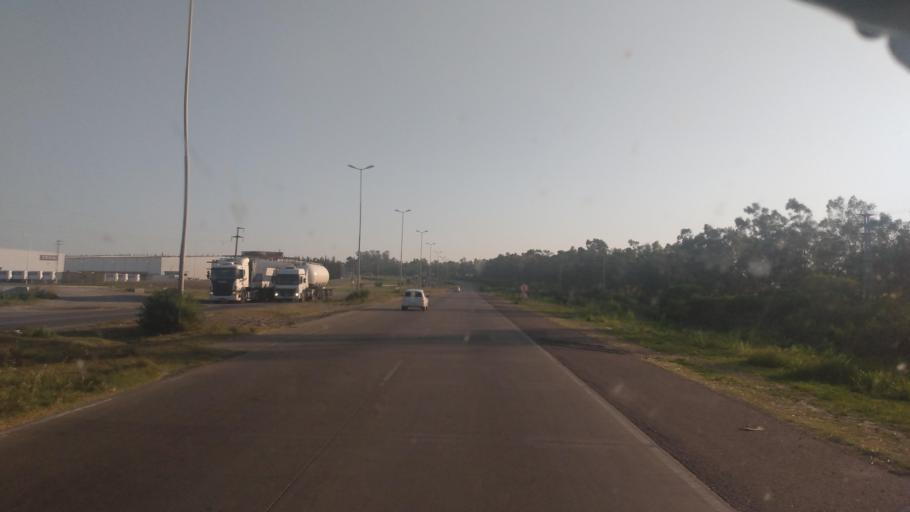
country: AR
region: Buenos Aires
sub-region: Partido de Campana
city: Campana
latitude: -34.2380
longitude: -58.9635
